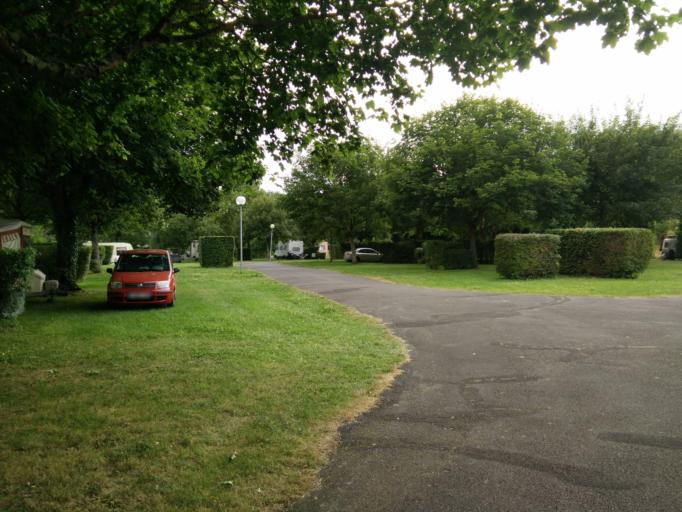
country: FR
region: Centre
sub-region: Departement d'Indre-et-Loire
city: Preuilly-sur-Claise
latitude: 46.8529
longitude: 0.9263
